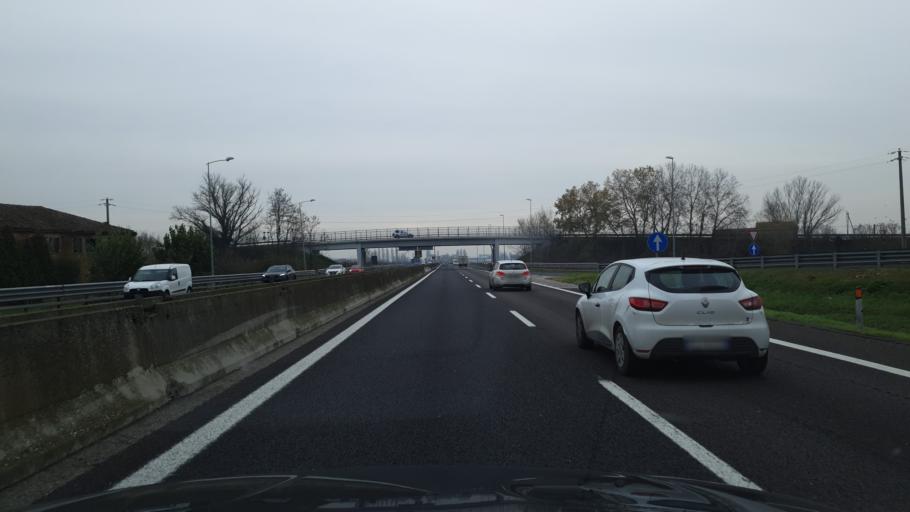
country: IT
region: Emilia-Romagna
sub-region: Provincia di Ferrara
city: San Martino
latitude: 44.7919
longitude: 11.5525
